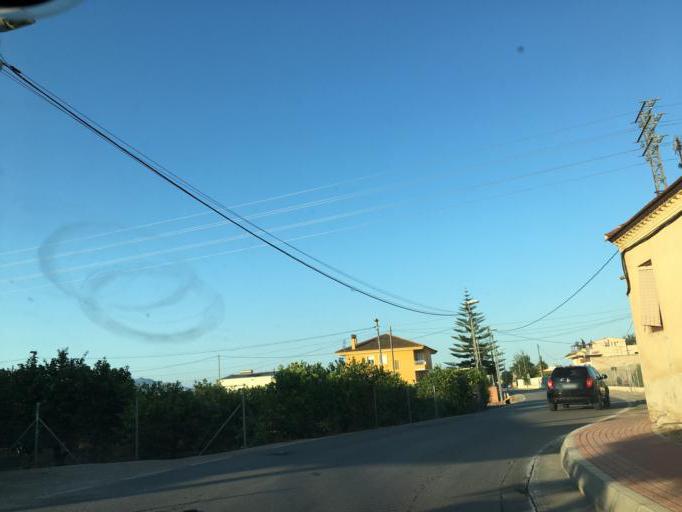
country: ES
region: Murcia
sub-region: Murcia
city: Murcia
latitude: 38.0080
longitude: -1.0765
